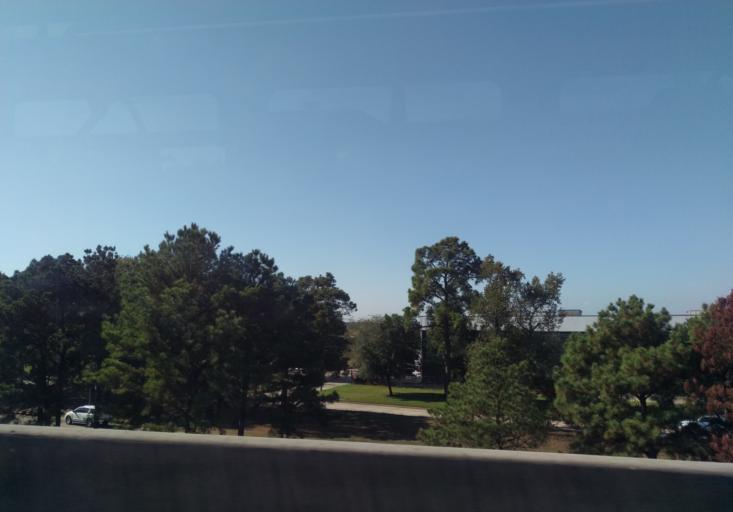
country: US
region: Texas
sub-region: Harris County
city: Aldine
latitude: 29.9703
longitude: -95.3390
